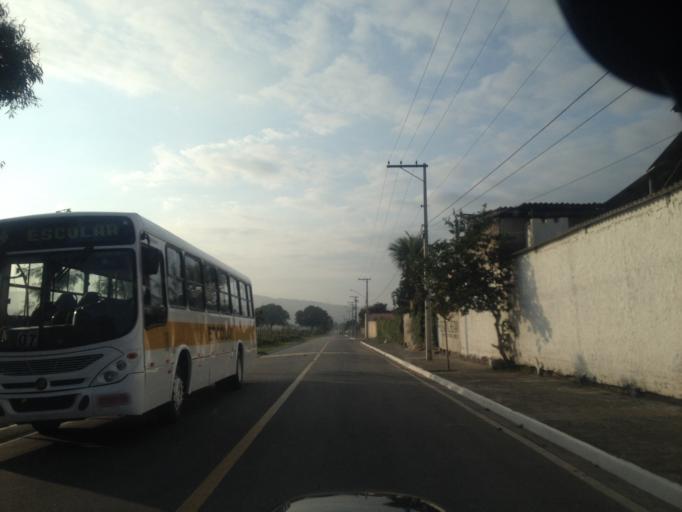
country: BR
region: Rio de Janeiro
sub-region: Porto Real
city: Porto Real
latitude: -22.4412
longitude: -44.3098
